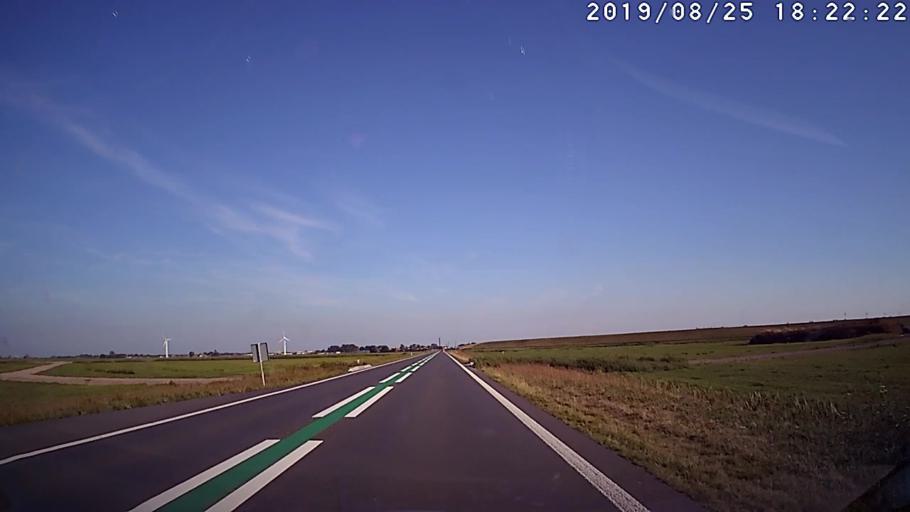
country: NL
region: Friesland
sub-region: Gemeente Lemsterland
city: Lemmer
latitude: 52.8660
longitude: 5.6483
